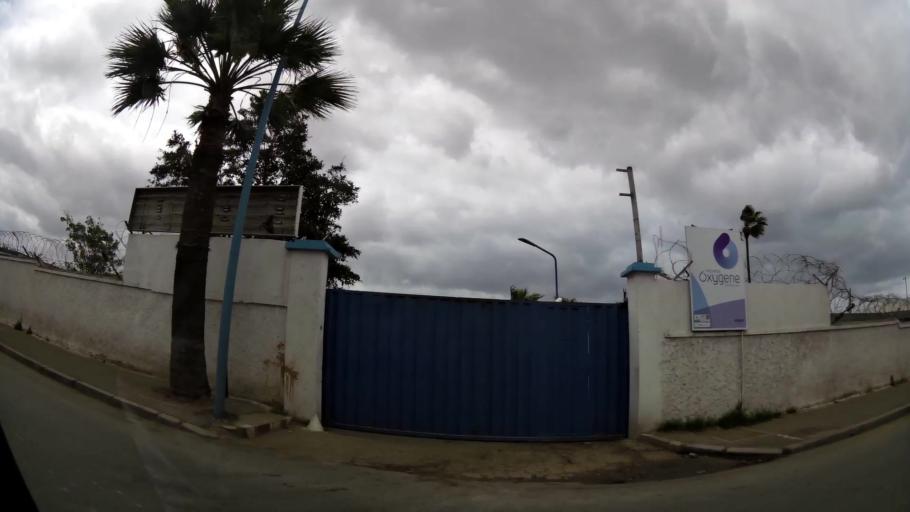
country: MA
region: Grand Casablanca
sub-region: Casablanca
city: Casablanca
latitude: 33.5903
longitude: -7.5458
